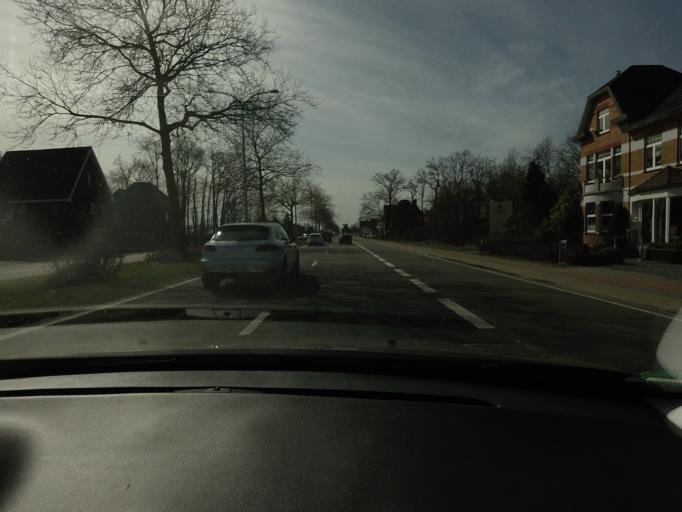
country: BE
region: Flanders
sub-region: Provincie Limburg
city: Zonhoven
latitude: 50.9689
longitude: 5.3592
